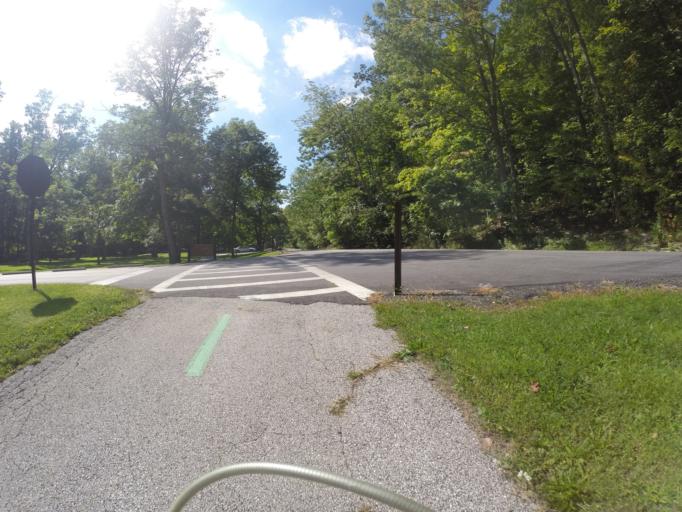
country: US
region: Ohio
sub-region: Cuyahoga County
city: Richmond Heights
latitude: 41.5616
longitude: -81.5327
